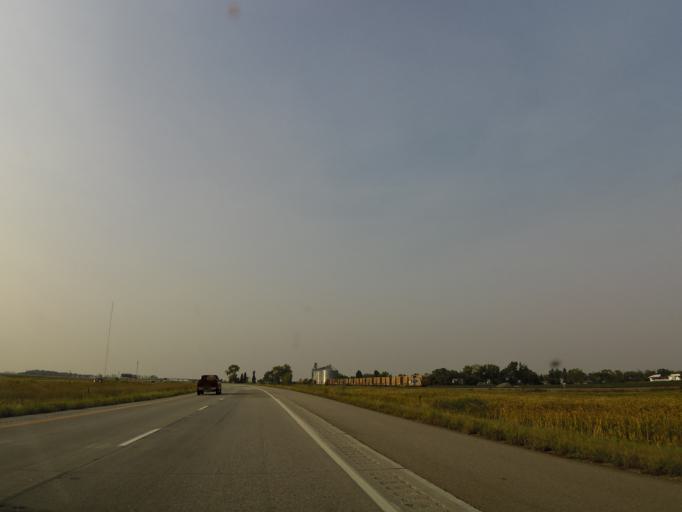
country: US
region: North Dakota
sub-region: Cass County
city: West Fargo
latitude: 47.1393
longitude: -96.9669
